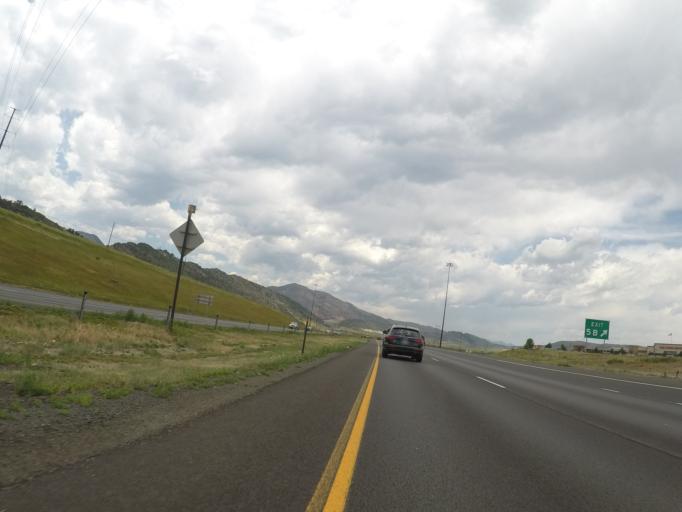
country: US
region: Colorado
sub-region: Jefferson County
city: Ken Caryl
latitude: 39.6320
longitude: -105.1599
